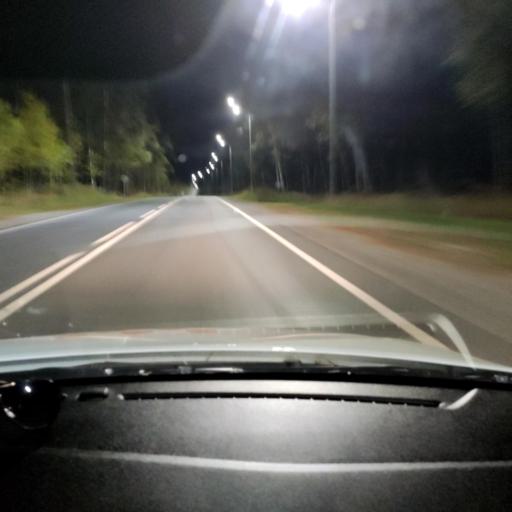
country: RU
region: Tatarstan
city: Stolbishchi
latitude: 55.6352
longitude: 49.0756
